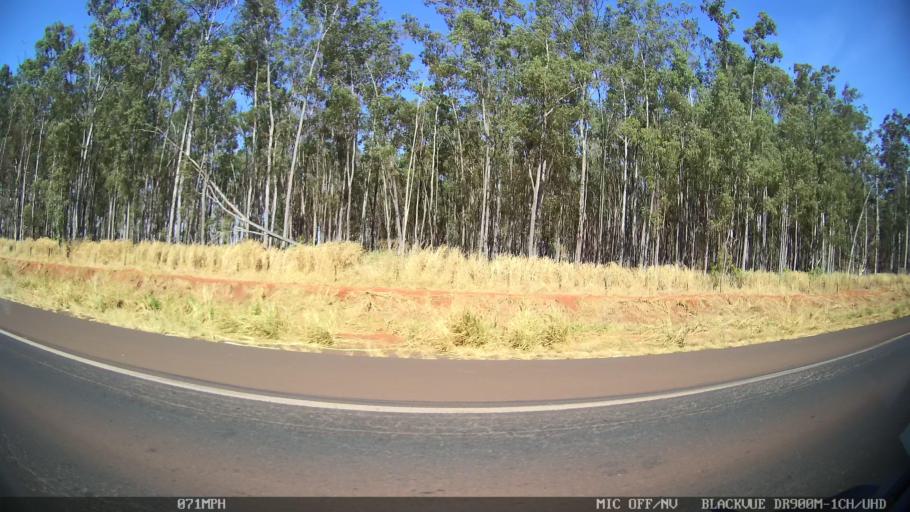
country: BR
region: Sao Paulo
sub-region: Barretos
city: Barretos
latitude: -20.4923
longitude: -48.5251
